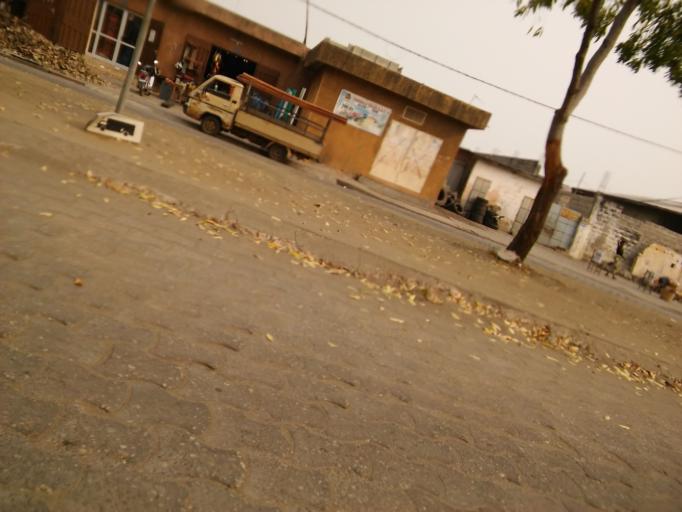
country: BJ
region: Littoral
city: Cotonou
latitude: 6.3774
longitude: 2.4073
